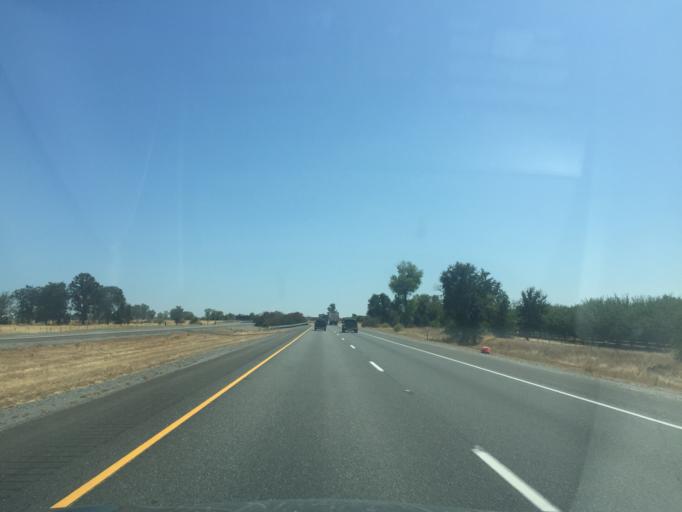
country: US
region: California
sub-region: Tehama County
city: Gerber
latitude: 40.0118
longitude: -122.2079
